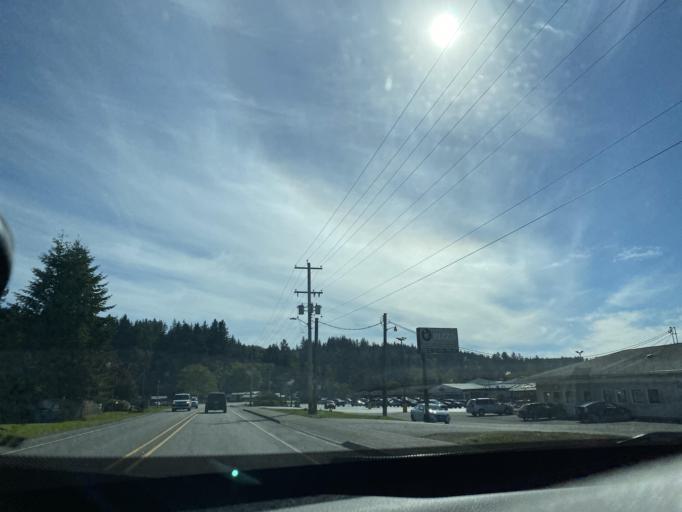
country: US
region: Washington
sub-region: Clallam County
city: Forks
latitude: 47.9430
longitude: -124.3855
